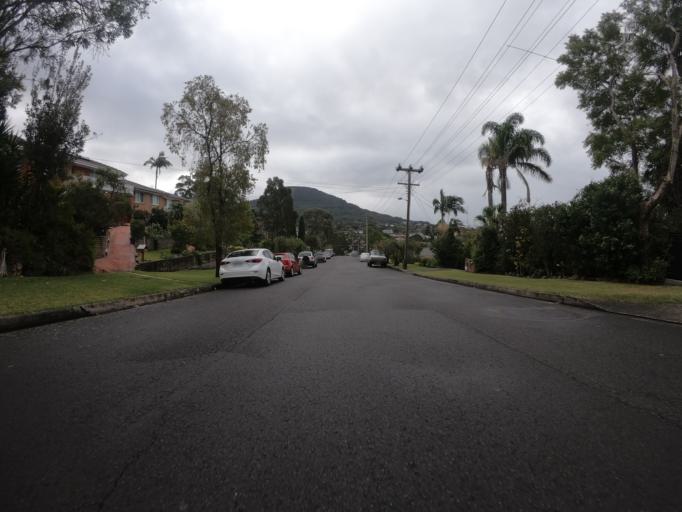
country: AU
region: New South Wales
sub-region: Wollongong
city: Mount Keira
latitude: -34.4277
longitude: 150.8553
